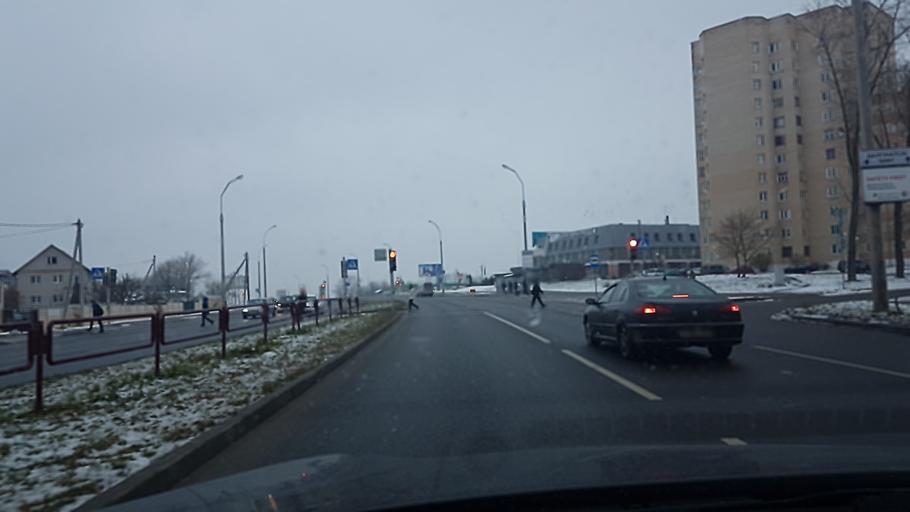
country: BY
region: Minsk
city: Bal'shavik
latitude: 53.9580
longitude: 27.5362
